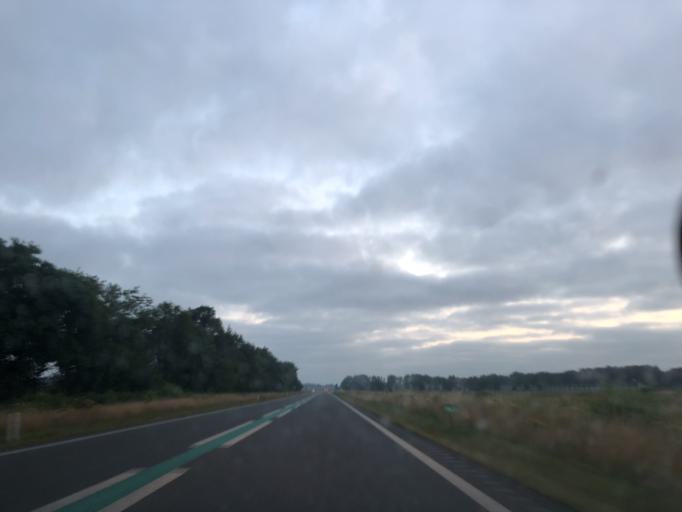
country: NL
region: Drenthe
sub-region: Gemeente Borger-Odoorn
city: Borger
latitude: 52.9674
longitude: 6.7784
